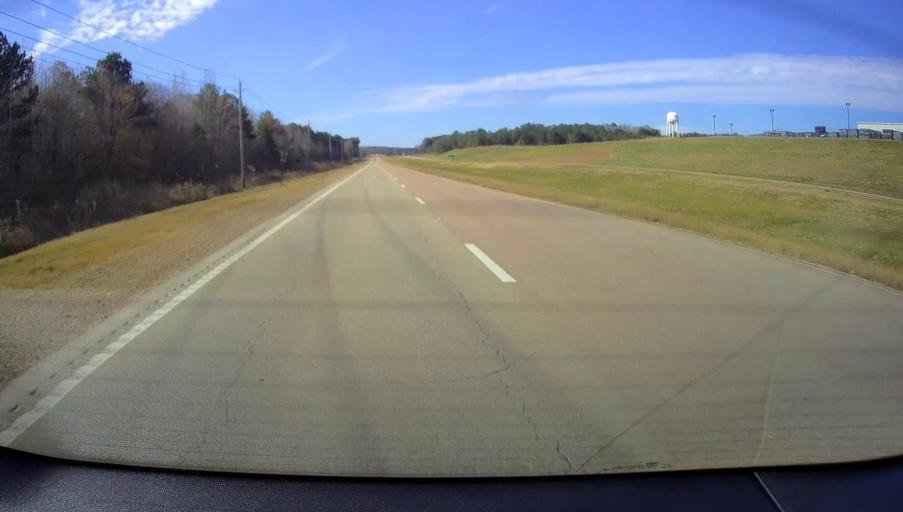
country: US
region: Mississippi
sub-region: Tippah County
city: Ripley
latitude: 34.9506
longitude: -88.9307
